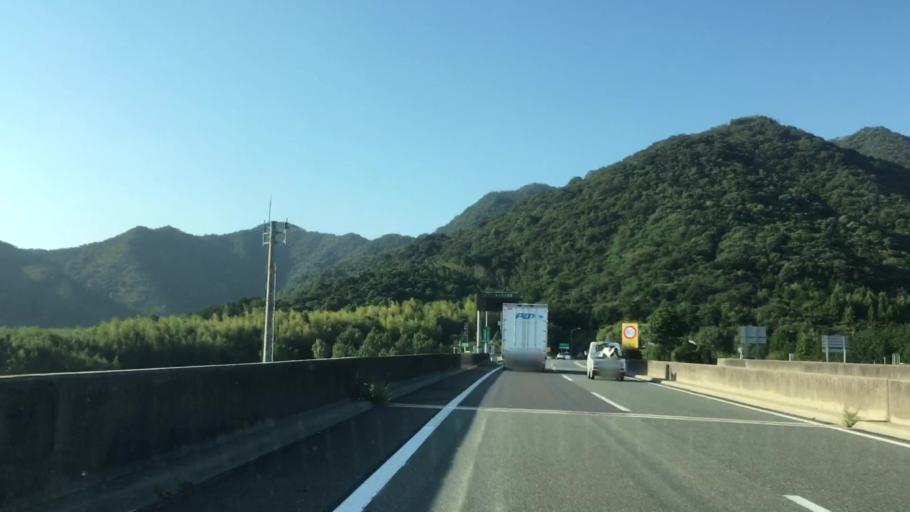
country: JP
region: Yamaguchi
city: Ogori-shimogo
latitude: 34.0979
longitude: 131.4521
